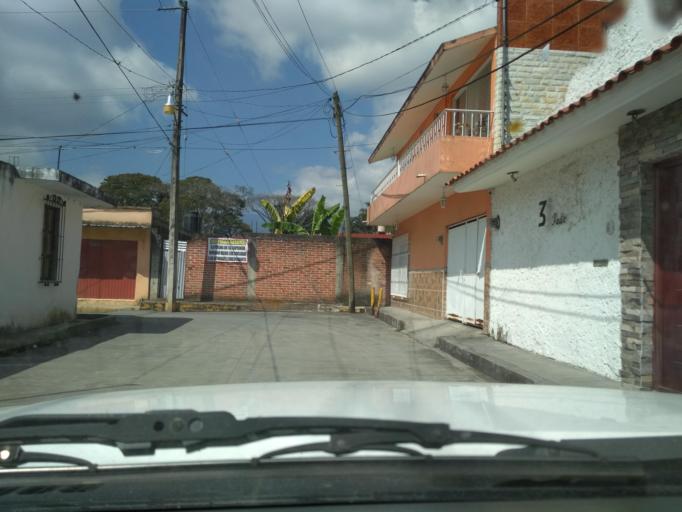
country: MX
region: Veracruz
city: Coatepec
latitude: 19.4498
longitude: -96.9477
